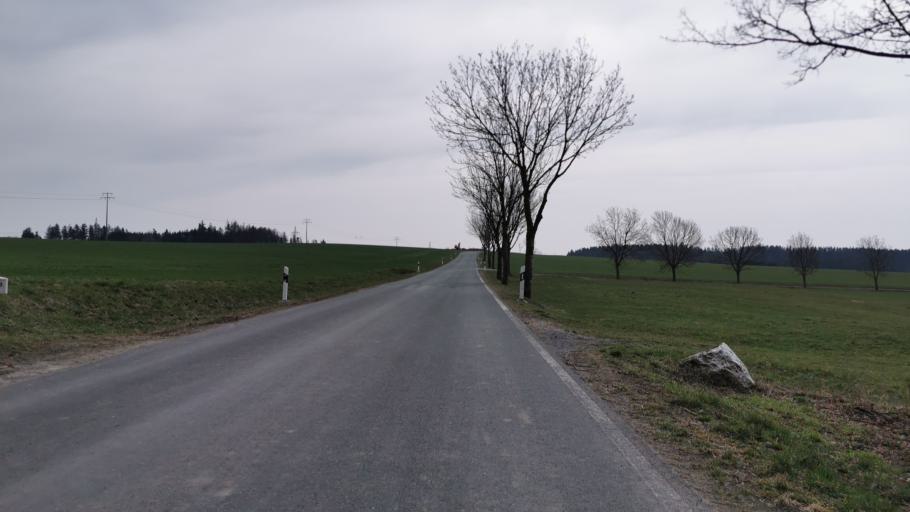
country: DE
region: Thuringia
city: Leutenberg
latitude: 50.5353
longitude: 11.4283
